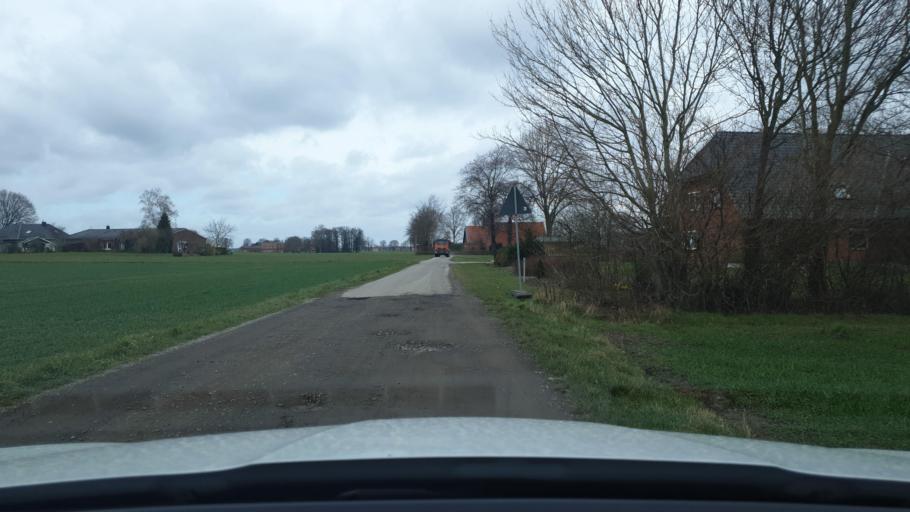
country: DE
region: North Rhine-Westphalia
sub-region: Regierungsbezirk Detmold
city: Hille
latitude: 52.3352
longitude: 8.7580
